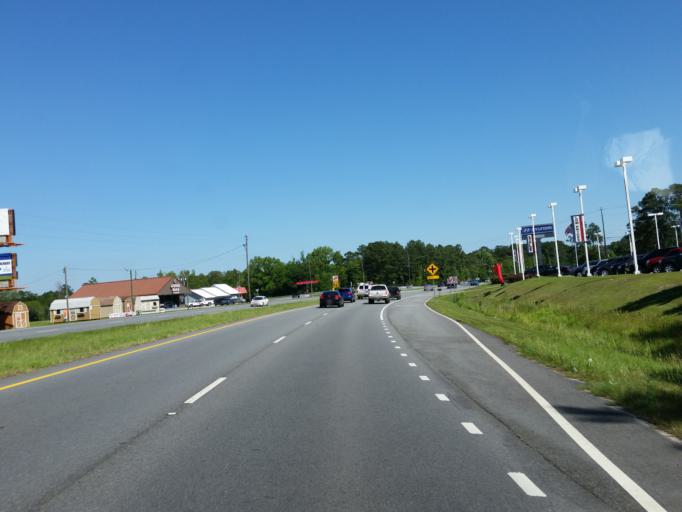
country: US
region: Georgia
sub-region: Lowndes County
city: Remerton
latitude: 30.8968
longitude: -83.3233
